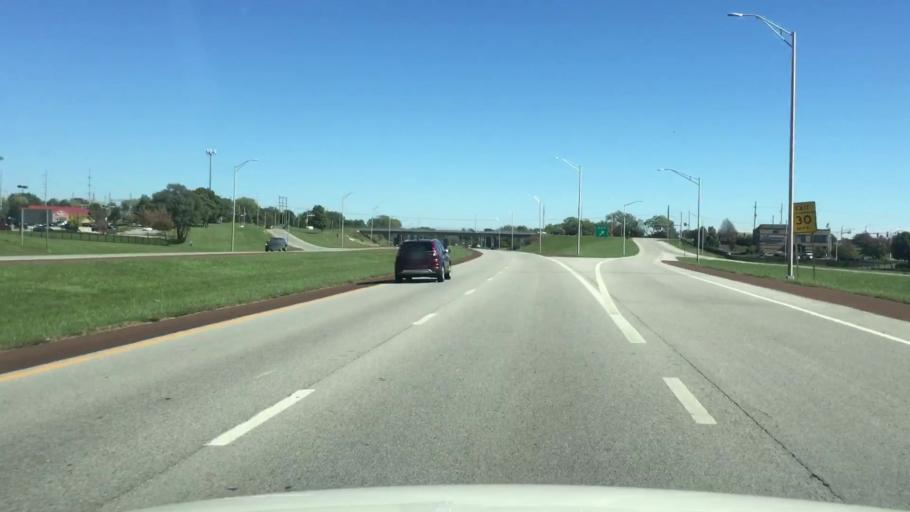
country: US
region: Kansas
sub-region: Johnson County
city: Shawnee
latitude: 39.0082
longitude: -94.7655
